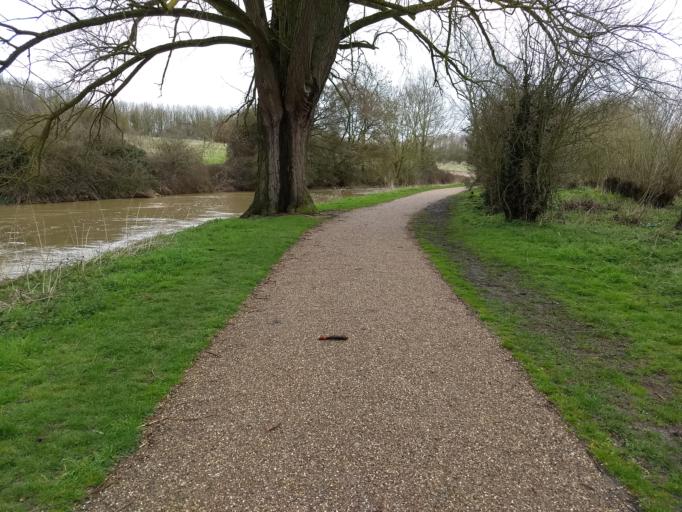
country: GB
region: England
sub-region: Milton Keynes
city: Stony Stratford
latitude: 52.0636
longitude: -0.8581
